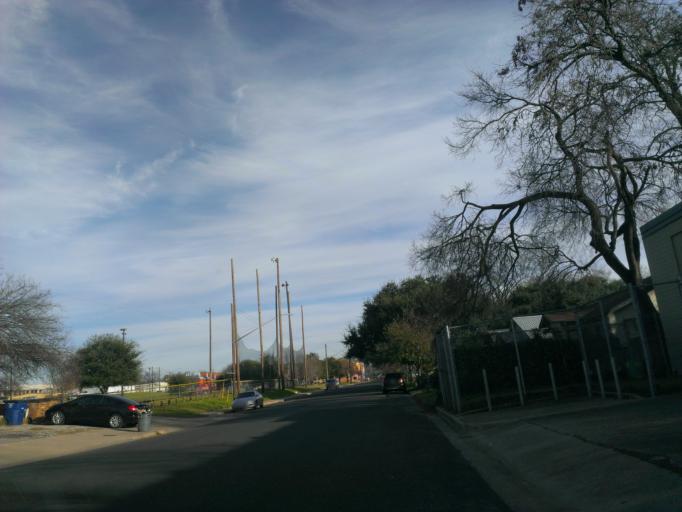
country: US
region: Texas
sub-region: Travis County
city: Austin
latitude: 30.2587
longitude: -97.7237
